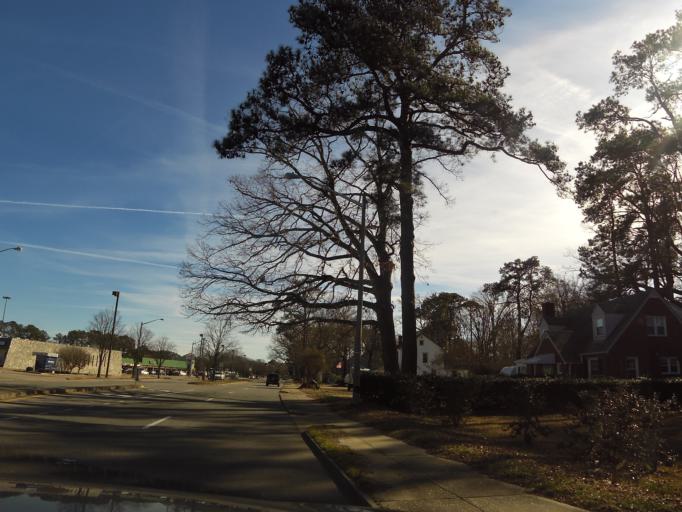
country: US
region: Virginia
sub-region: City of Newport News
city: Newport News
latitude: 37.0414
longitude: -76.4712
